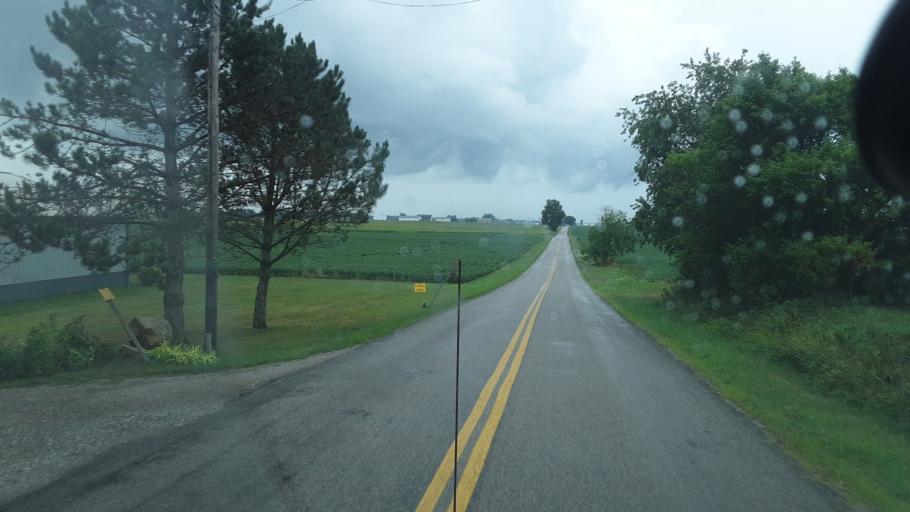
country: US
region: Ohio
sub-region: Williams County
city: Edgerton
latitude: 41.5663
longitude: -84.7884
